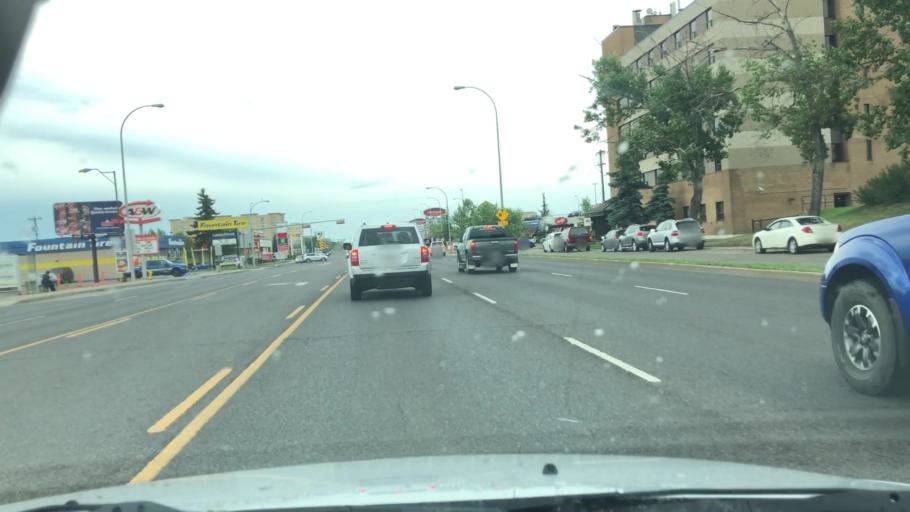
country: CA
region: Alberta
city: Edmonton
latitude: 53.5954
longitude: -113.4919
